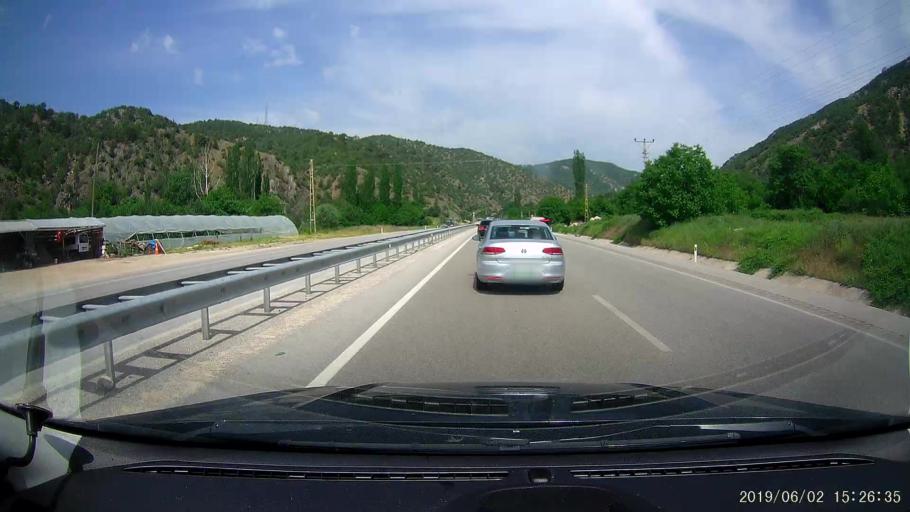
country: TR
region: Amasya
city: Saraycik
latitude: 40.9864
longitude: 35.0399
